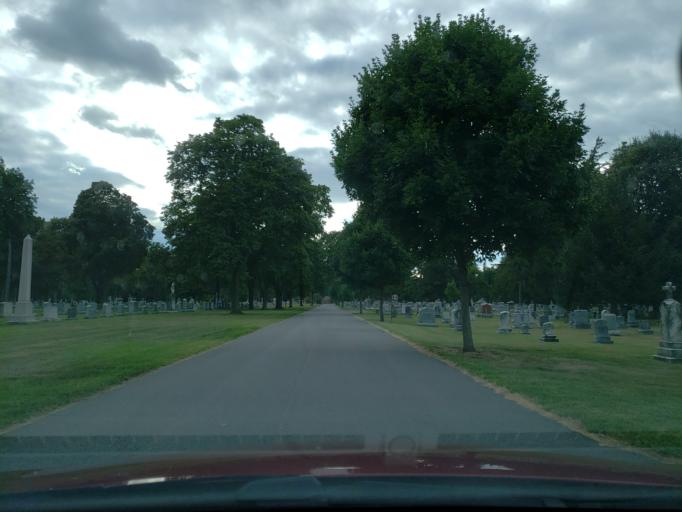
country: US
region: New York
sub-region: Monroe County
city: Irondequoit
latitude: 43.2136
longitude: -77.6331
